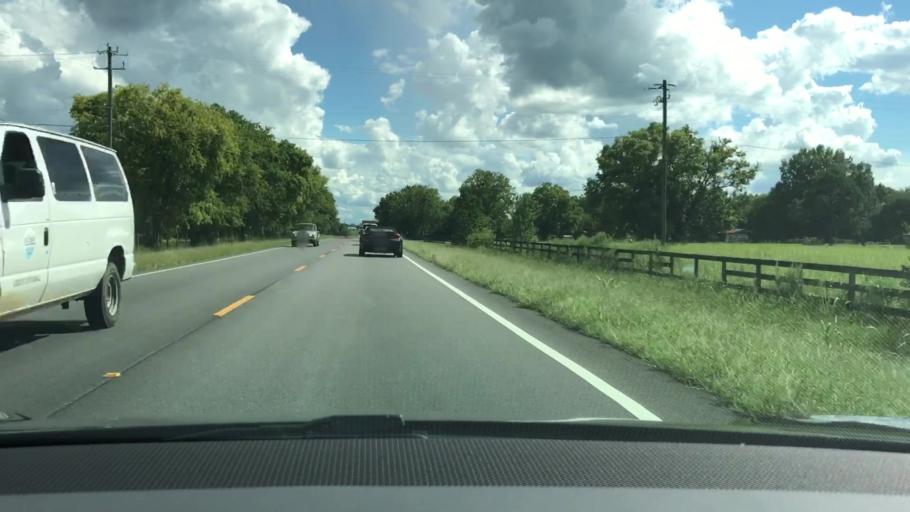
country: US
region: Alabama
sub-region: Montgomery County
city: Pike Road
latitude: 32.3047
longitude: -86.1027
